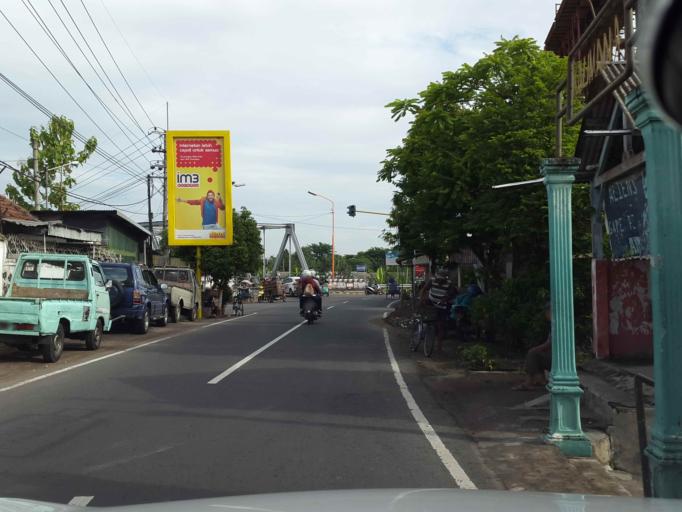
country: ID
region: East Java
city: Mojokerto
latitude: -7.4634
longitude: 112.4290
